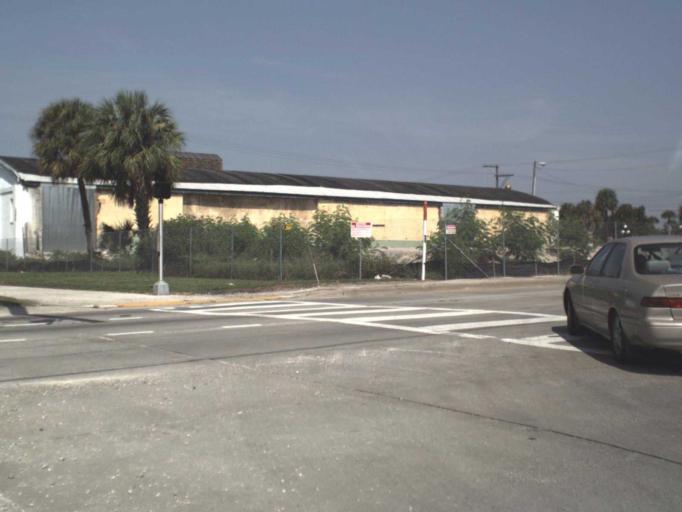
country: US
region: Florida
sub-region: Hillsborough County
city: Tampa
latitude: 27.9559
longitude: -82.4346
